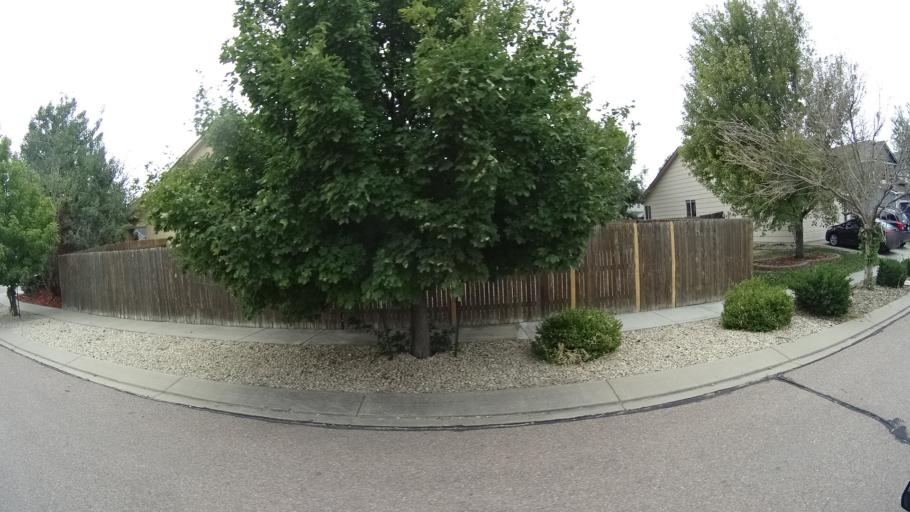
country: US
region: Colorado
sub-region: El Paso County
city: Cimarron Hills
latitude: 38.9175
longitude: -104.6897
